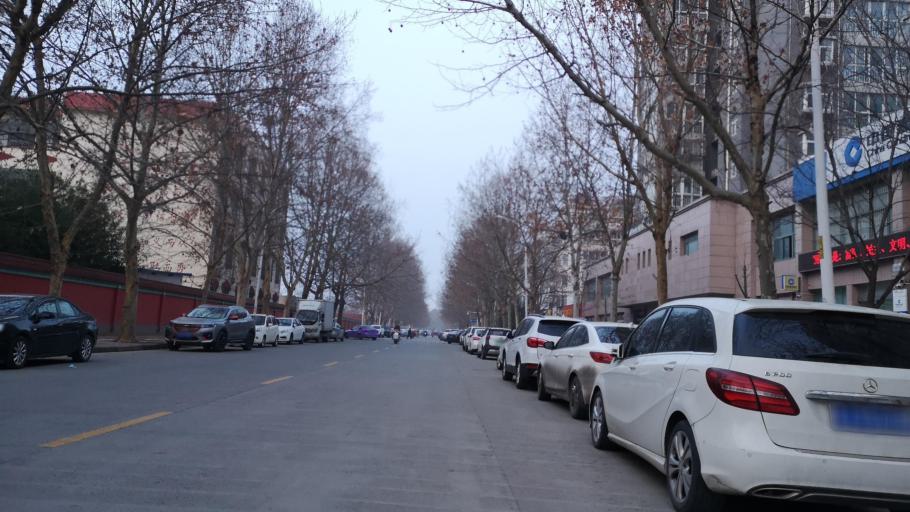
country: CN
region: Henan Sheng
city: Zhongyuanlu
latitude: 35.7539
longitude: 115.0608
